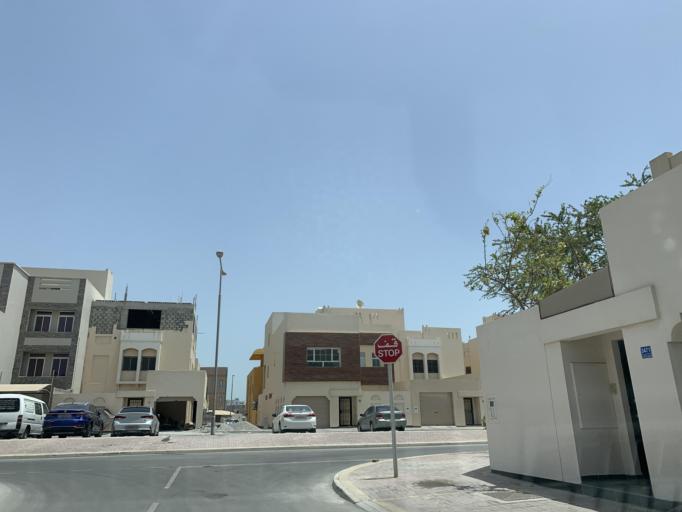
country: BH
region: Northern
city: Sitrah
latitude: 26.1395
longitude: 50.5934
